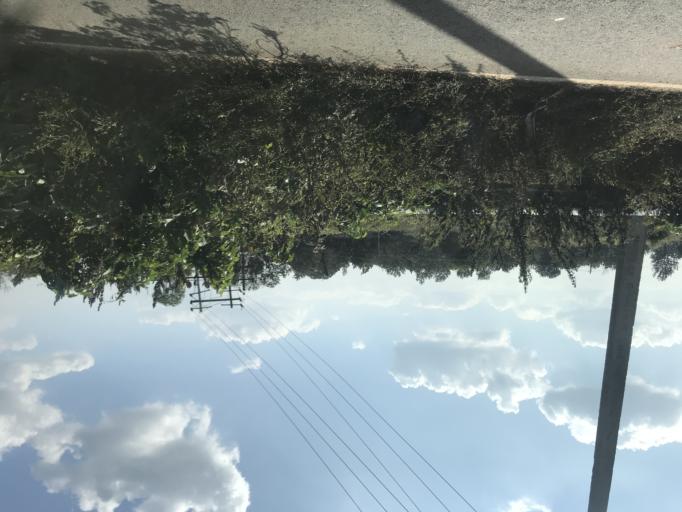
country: IN
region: Karnataka
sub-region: Bangalore Urban
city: Anekal
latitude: 12.8039
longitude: 77.5602
